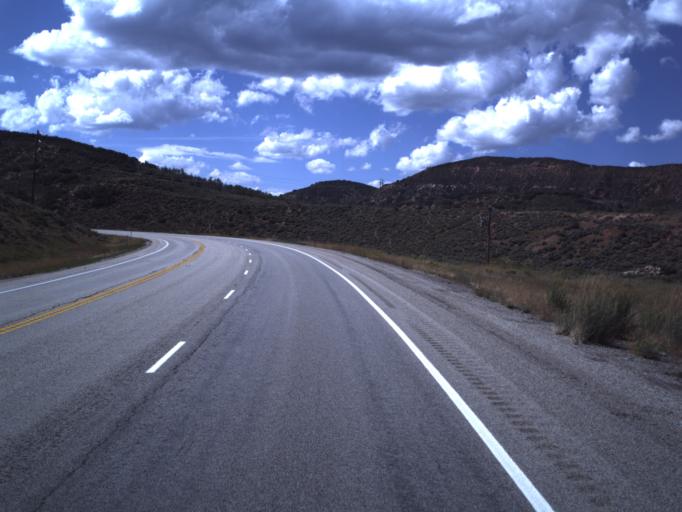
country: US
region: Utah
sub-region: Summit County
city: Francis
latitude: 40.2030
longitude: -110.9701
